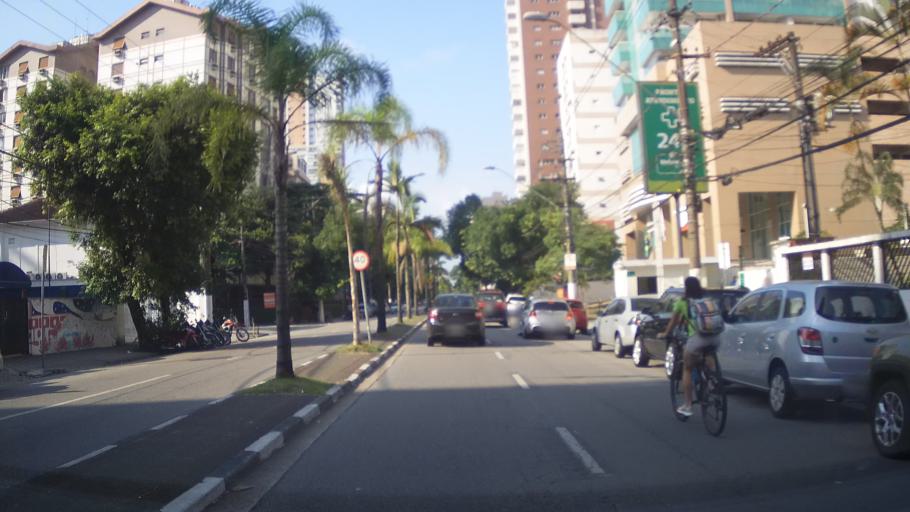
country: BR
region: Sao Paulo
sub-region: Santos
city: Santos
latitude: -23.9669
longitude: -46.3238
